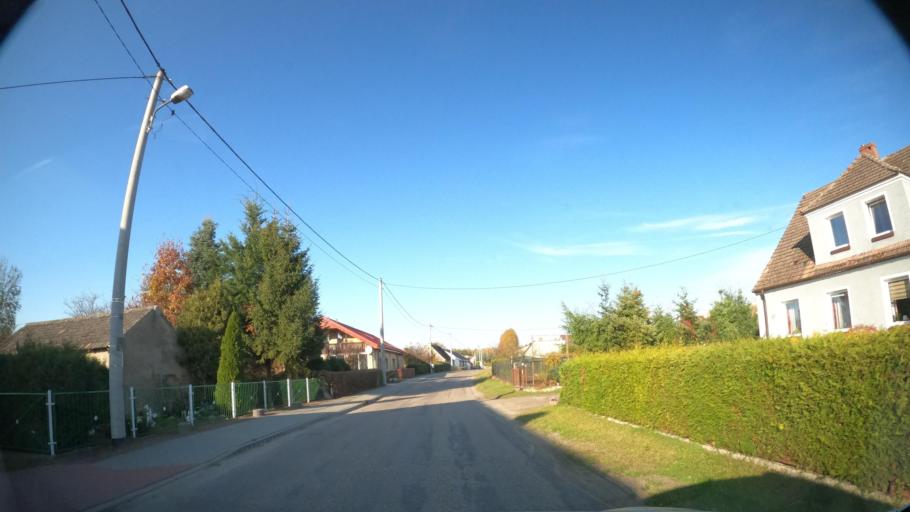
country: PL
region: Greater Poland Voivodeship
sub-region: Powiat zlotowski
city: Sypniewo
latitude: 53.3508
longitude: 16.5727
